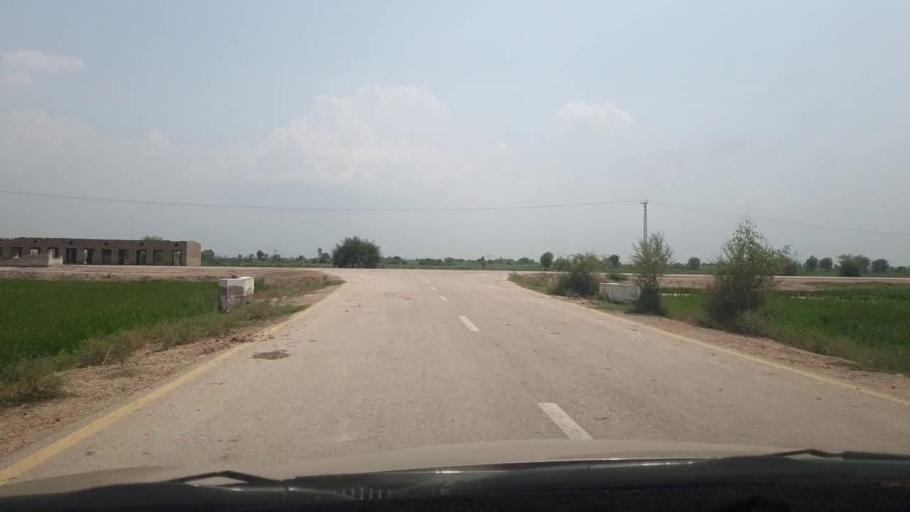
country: PK
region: Sindh
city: Naudero
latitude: 27.6950
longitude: 68.3335
